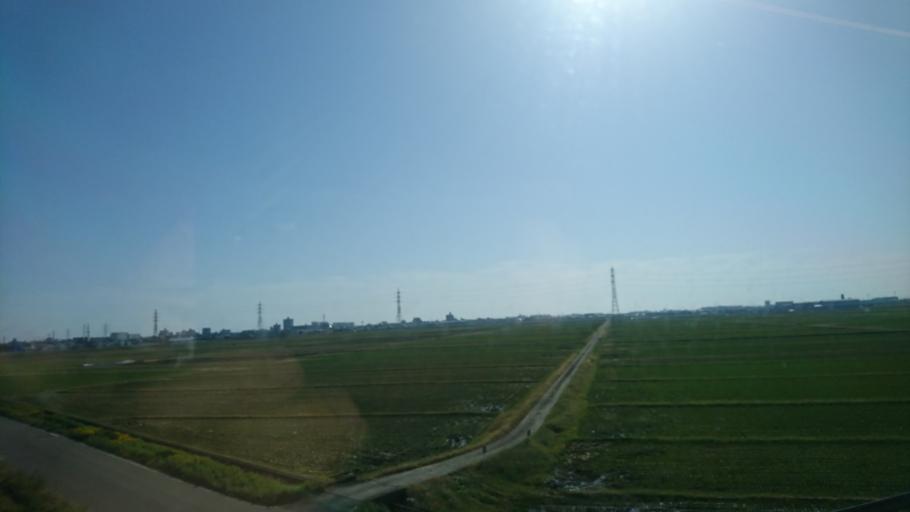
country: JP
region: Miyagi
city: Rifu
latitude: 38.2925
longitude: 140.9478
